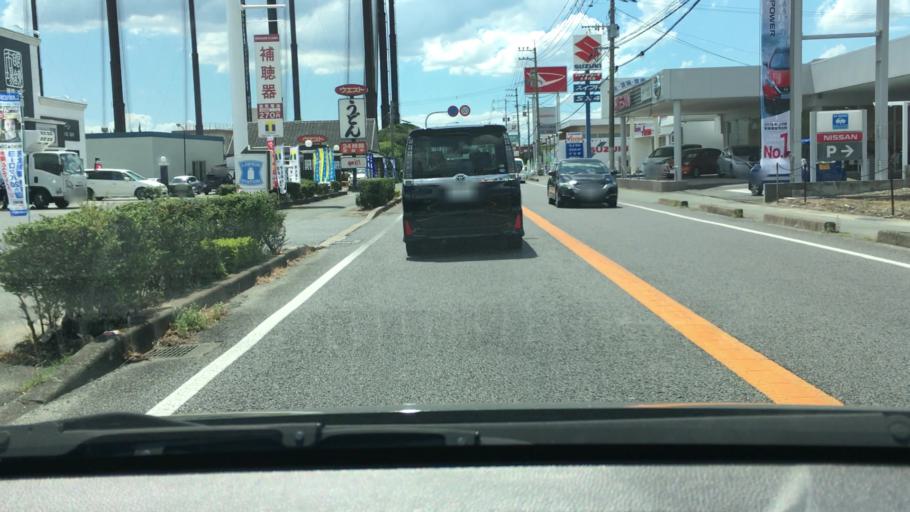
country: JP
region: Saga Prefecture
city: Kanzakimachi-kanzaki
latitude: 33.3235
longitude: 130.3985
